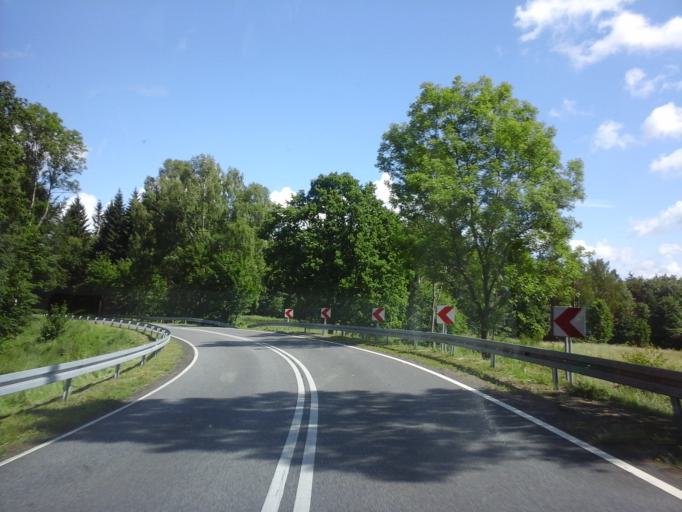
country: PL
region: West Pomeranian Voivodeship
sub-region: Powiat stargardzki
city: Insko
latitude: 53.4801
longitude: 15.5818
